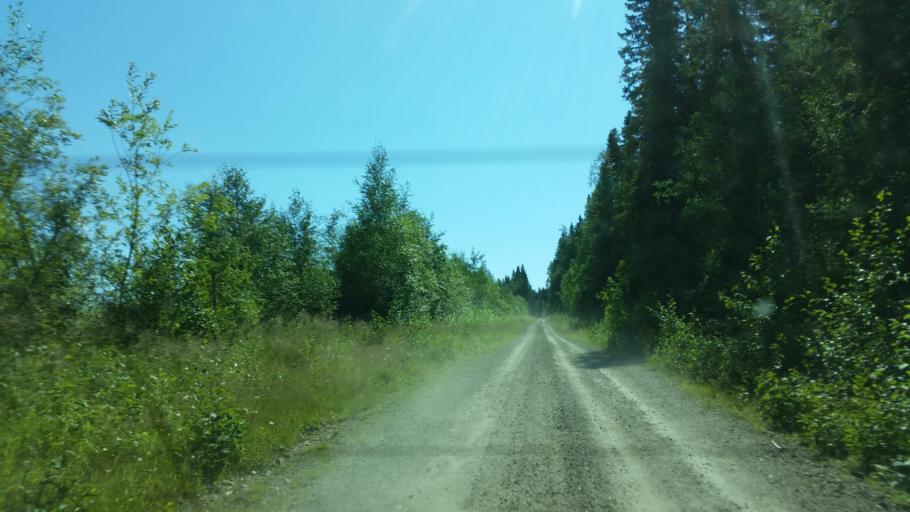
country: SE
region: Vaesternorrland
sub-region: Ange Kommun
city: Ange
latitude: 62.2070
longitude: 15.4336
